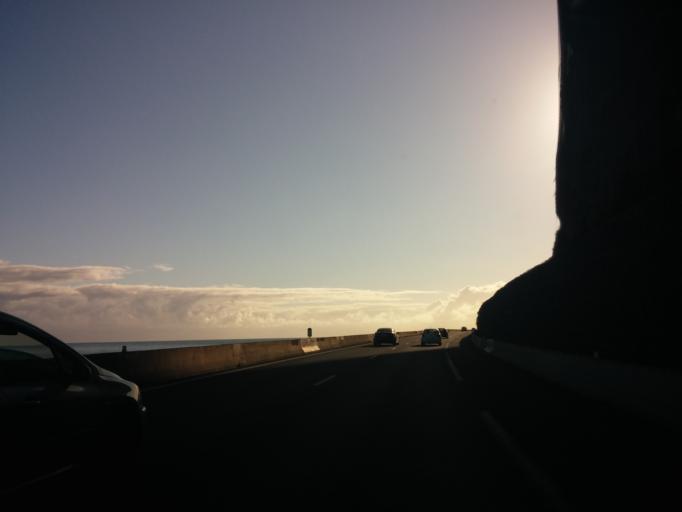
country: RE
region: Reunion
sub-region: Reunion
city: La Possession
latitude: -20.9005
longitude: 55.3685
